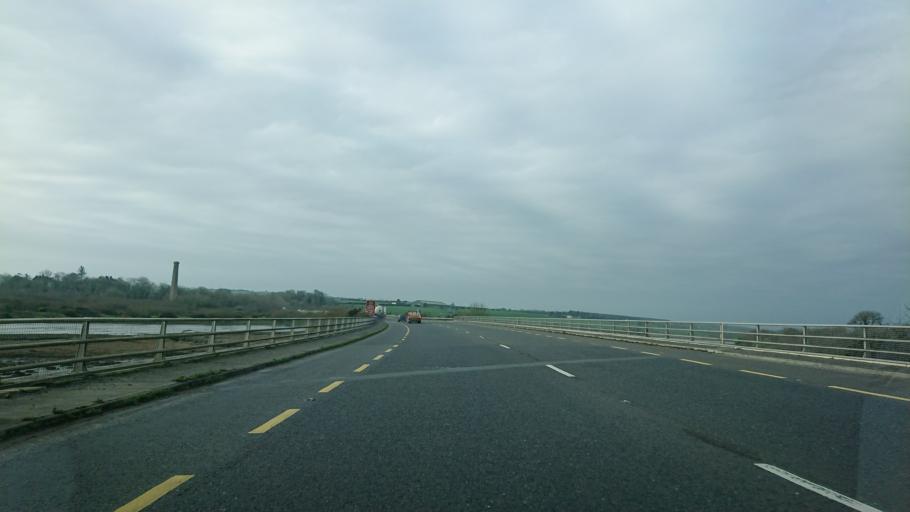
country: IE
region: Munster
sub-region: County Cork
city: Youghal
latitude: 51.9756
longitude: -7.8687
